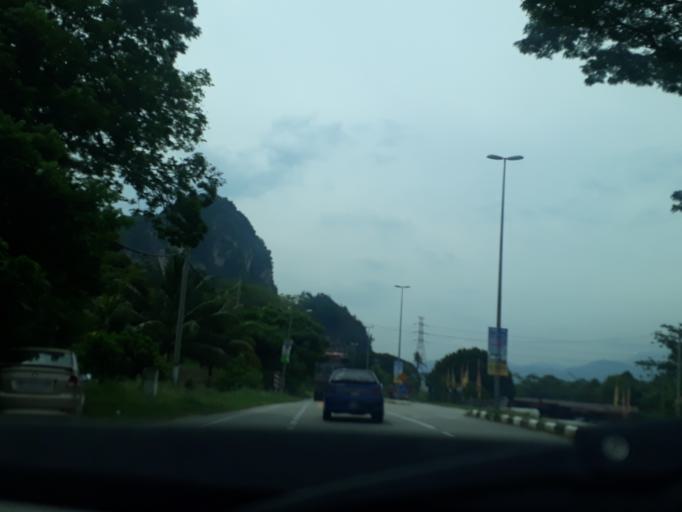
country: MY
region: Perak
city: Ipoh
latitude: 4.6389
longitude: 101.1549
